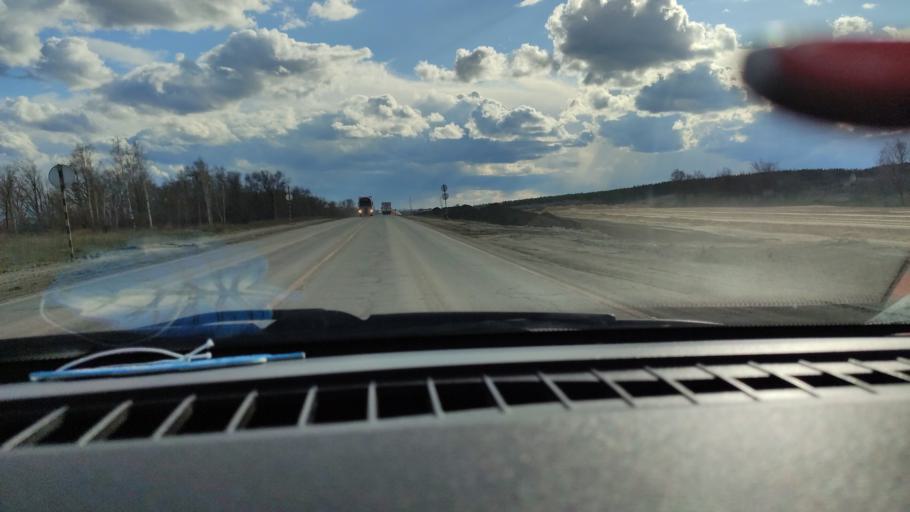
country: RU
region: Saratov
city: Sinodskoye
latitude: 52.0165
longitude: 46.6989
